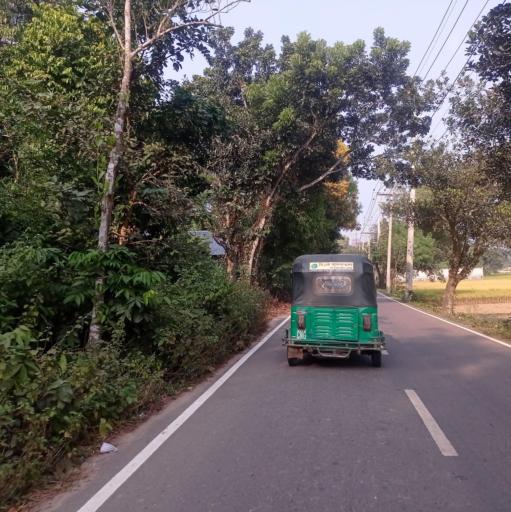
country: BD
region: Dhaka
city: Bhairab Bazar
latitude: 24.0760
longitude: 90.8467
